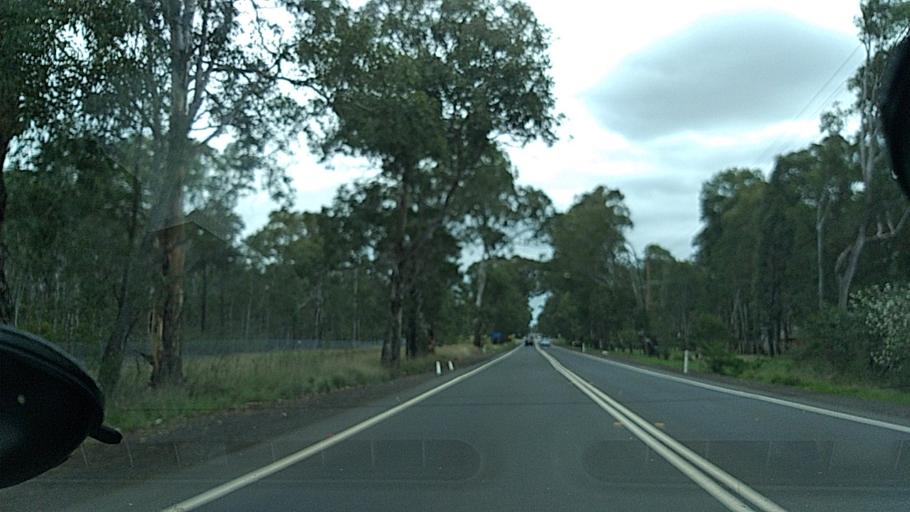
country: AU
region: New South Wales
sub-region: Hawkesbury
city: South Windsor
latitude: -33.6447
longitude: 150.7828
